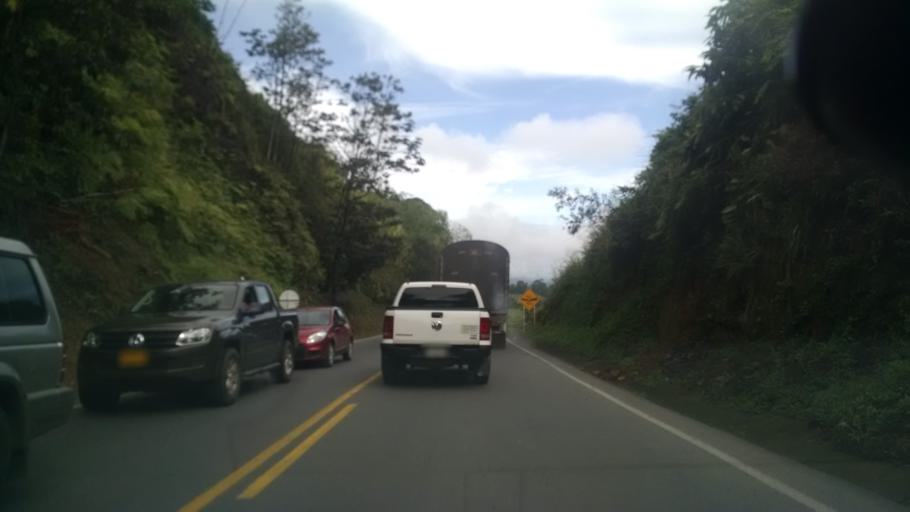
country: CO
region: Caldas
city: Palestina
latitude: 5.0760
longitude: -75.6467
